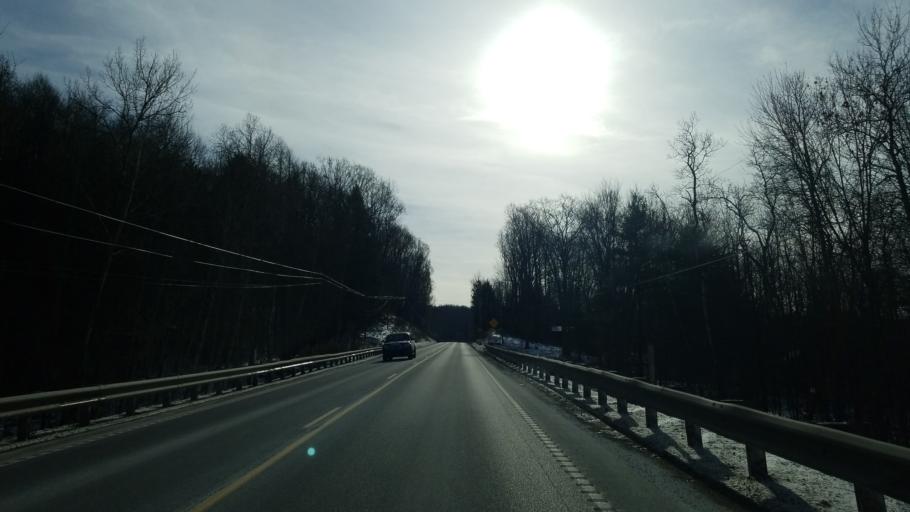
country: US
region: Pennsylvania
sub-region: Clearfield County
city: Treasure Lake
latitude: 41.1653
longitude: -78.5485
